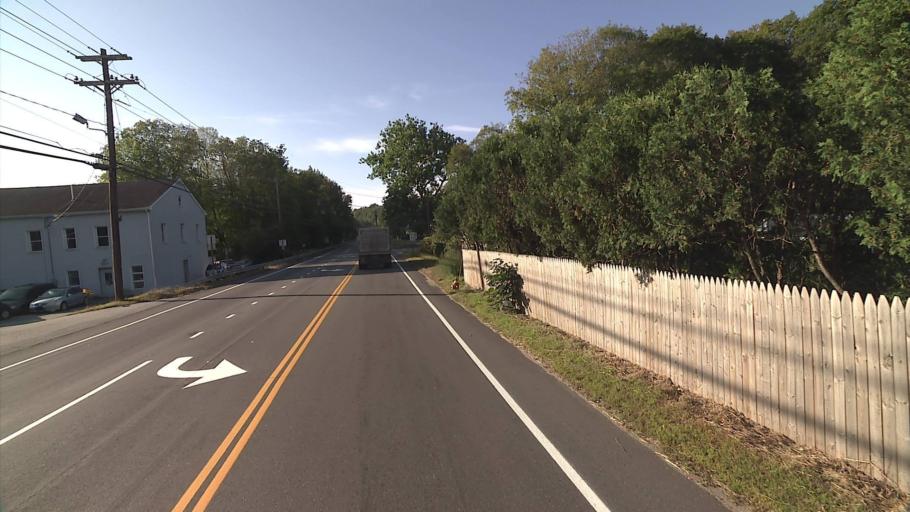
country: US
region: Connecticut
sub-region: Windham County
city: South Windham
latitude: 41.6792
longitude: -72.1688
